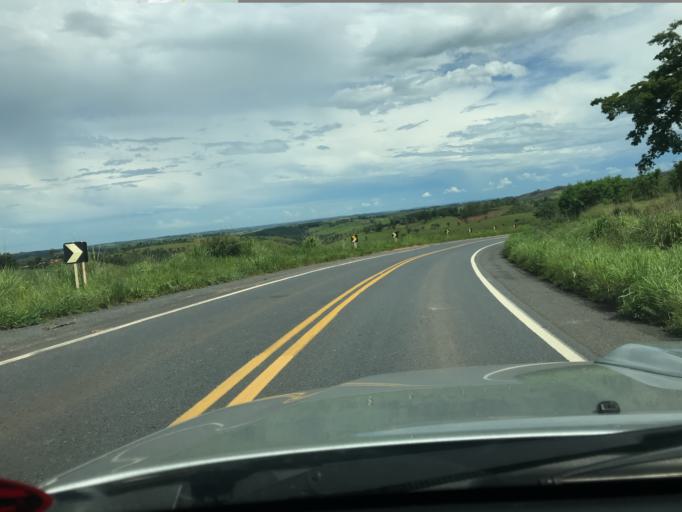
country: BR
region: Minas Gerais
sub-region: Campos Altos
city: Campos Altos
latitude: -19.7968
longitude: -46.0338
